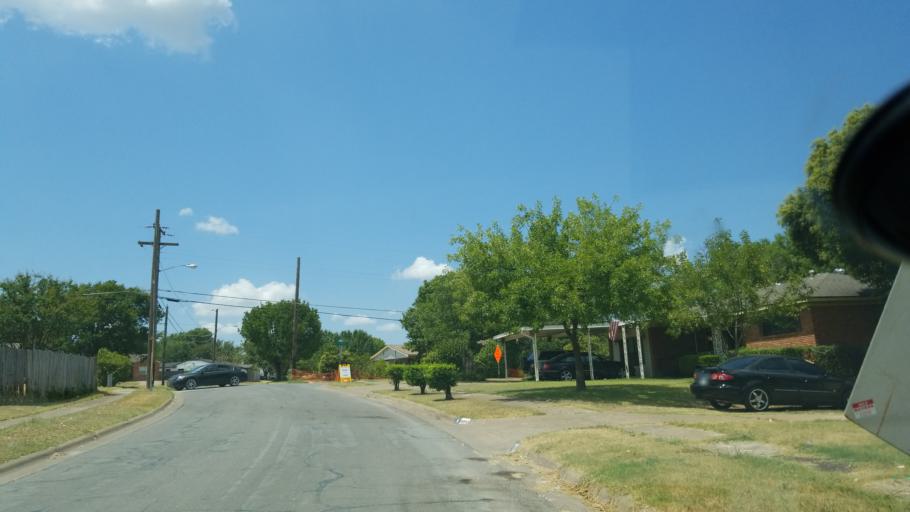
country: US
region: Texas
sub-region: Dallas County
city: Cockrell Hill
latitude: 32.7183
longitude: -96.8932
